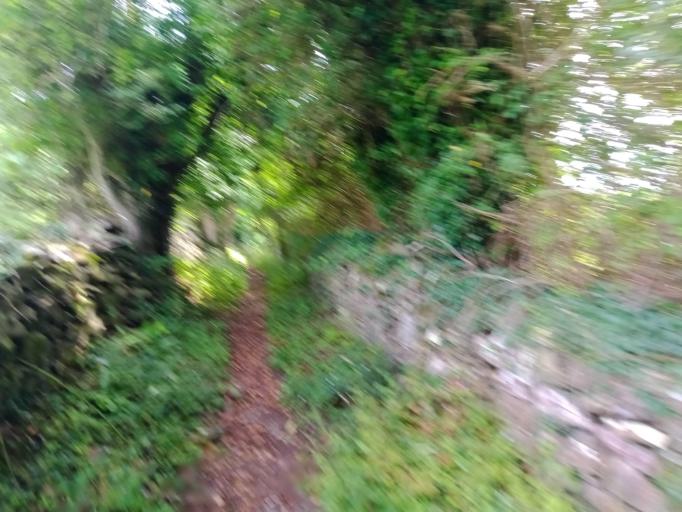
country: IE
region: Leinster
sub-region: Laois
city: Rathdowney
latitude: 52.8045
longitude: -7.4603
